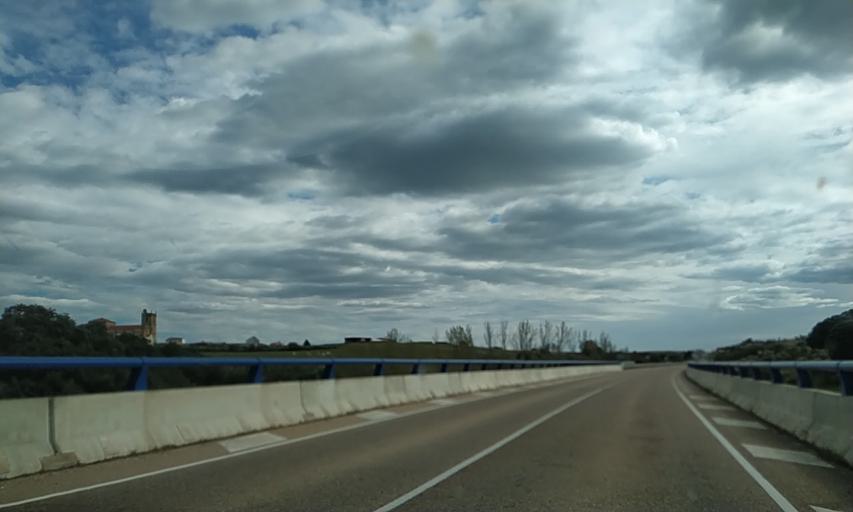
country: ES
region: Castille and Leon
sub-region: Provincia de Salamanca
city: Herguijuela de Ciudad Rodrigo
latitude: 40.4932
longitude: -6.5799
